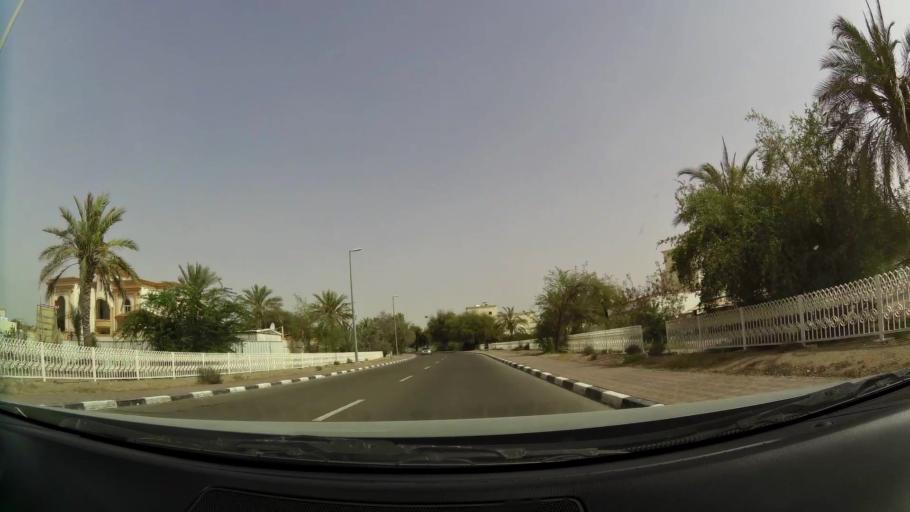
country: AE
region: Abu Dhabi
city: Al Ain
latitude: 24.1894
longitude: 55.6351
